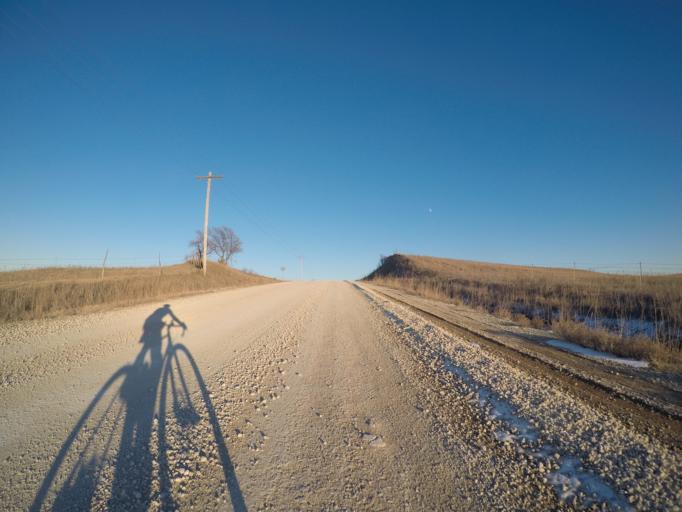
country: US
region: Kansas
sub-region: Pottawatomie County
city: Westmoreland
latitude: 39.3199
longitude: -96.5192
